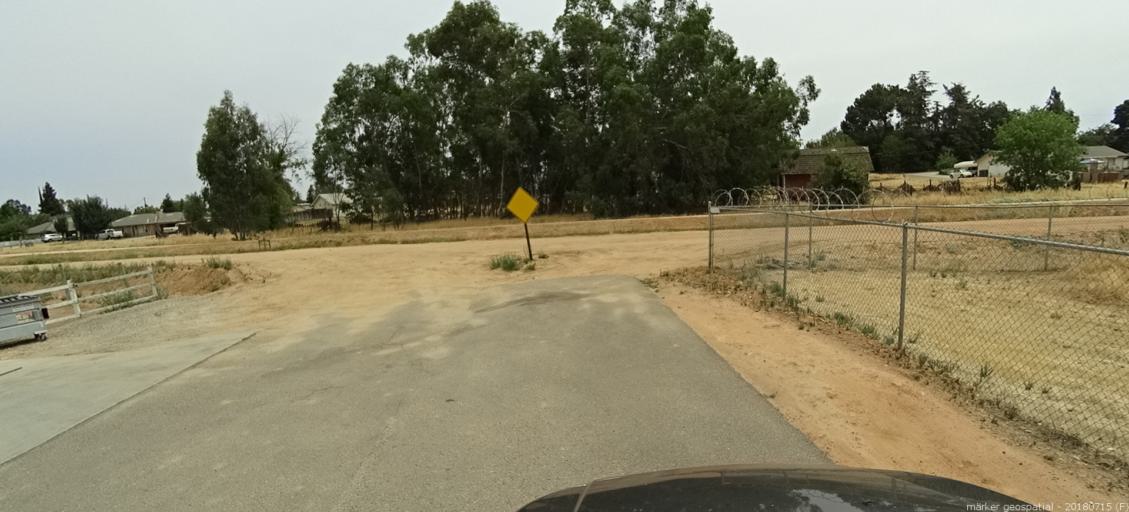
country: US
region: California
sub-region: Madera County
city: Madera Acres
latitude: 37.0109
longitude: -120.0874
